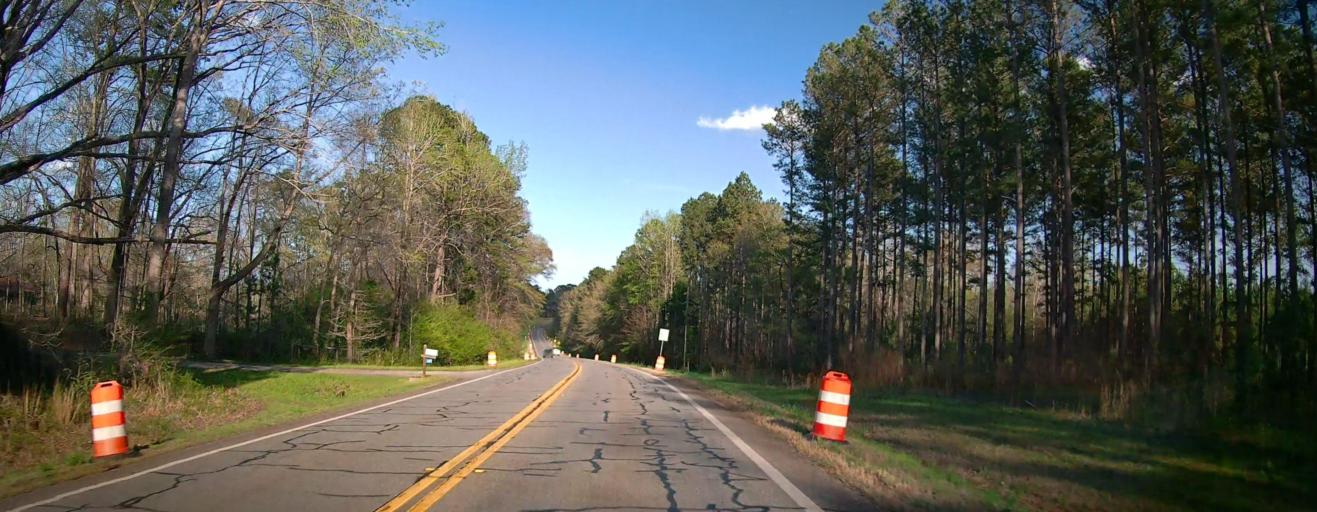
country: US
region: Georgia
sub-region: Baldwin County
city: Milledgeville
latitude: 33.1593
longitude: -83.3617
